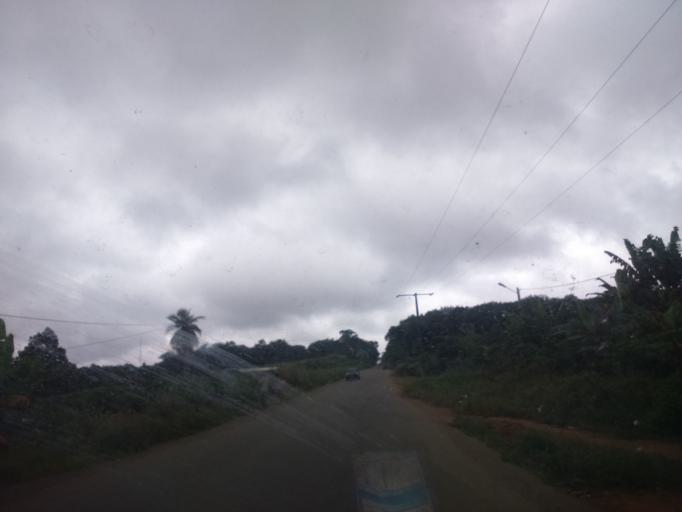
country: CI
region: Sud-Comoe
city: Bonoua
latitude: 5.2775
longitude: -3.5028
